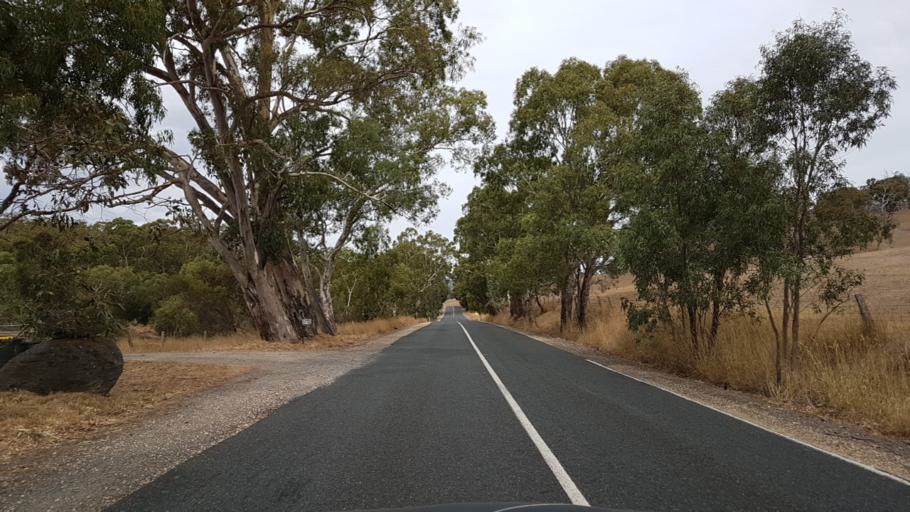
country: AU
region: South Australia
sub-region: Adelaide Hills
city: Birdwood
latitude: -34.7835
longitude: 138.9355
